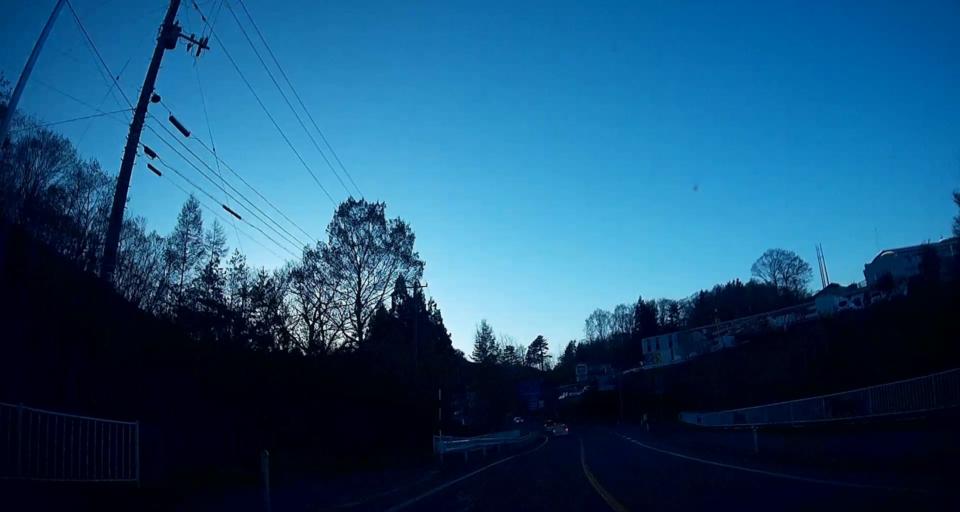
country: JP
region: Iwate
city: Miyako
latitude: 39.9300
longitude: 141.8942
